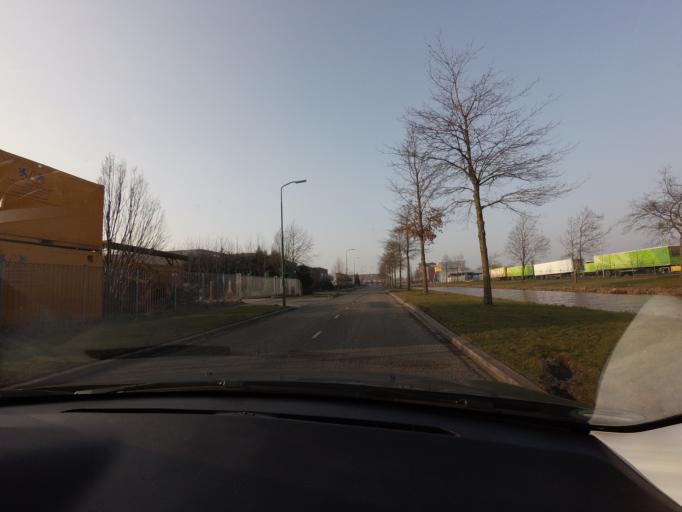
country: NL
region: Utrecht
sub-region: Gemeente Woerden
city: Woerden
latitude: 52.0767
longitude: 4.9091
